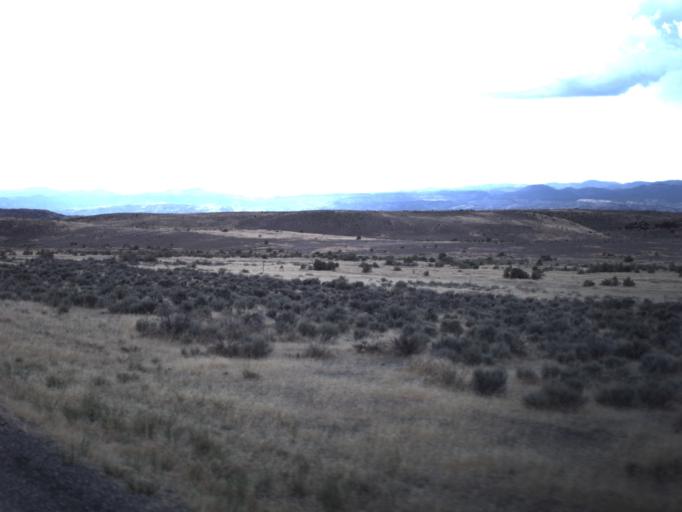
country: US
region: Utah
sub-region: Sevier County
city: Richfield
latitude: 38.7711
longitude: -111.9621
